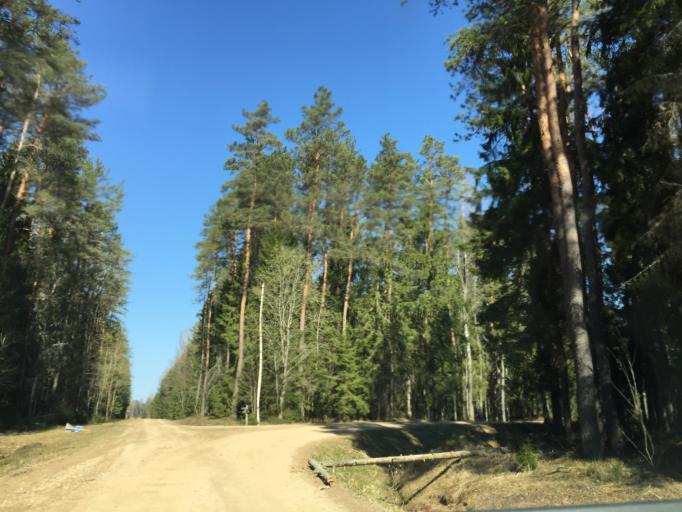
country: EE
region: Tartu
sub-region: Alatskivi vald
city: Kallaste
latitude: 58.5525
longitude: 26.9328
